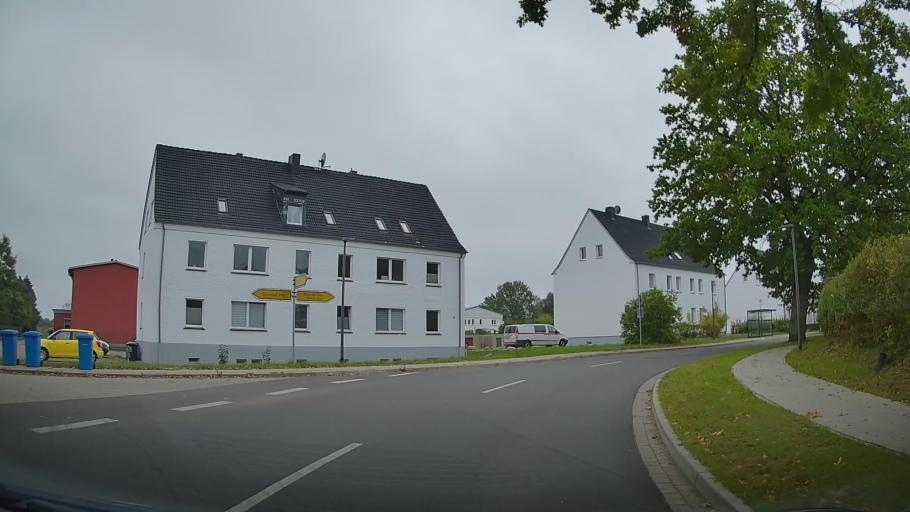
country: DE
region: Mecklenburg-Vorpommern
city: Guestrow
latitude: 53.8470
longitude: 12.1730
